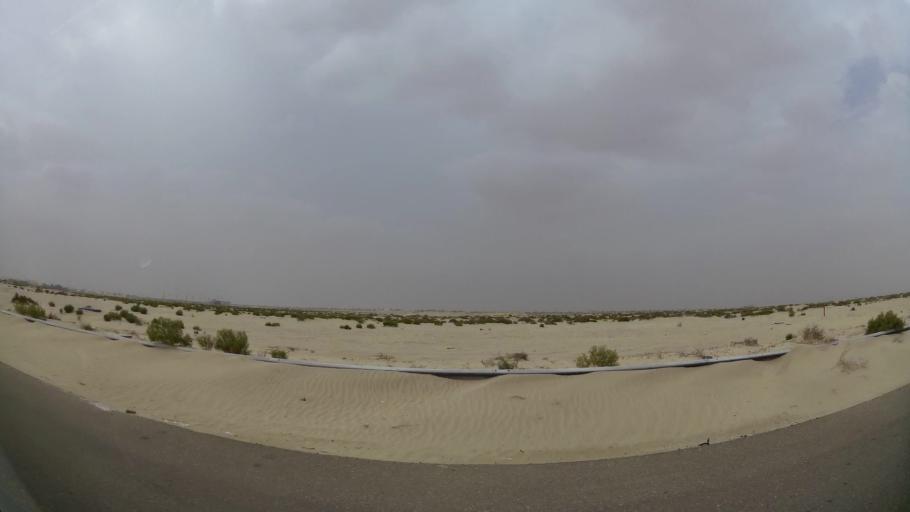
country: AE
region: Abu Dhabi
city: Abu Dhabi
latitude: 24.3837
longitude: 54.6781
